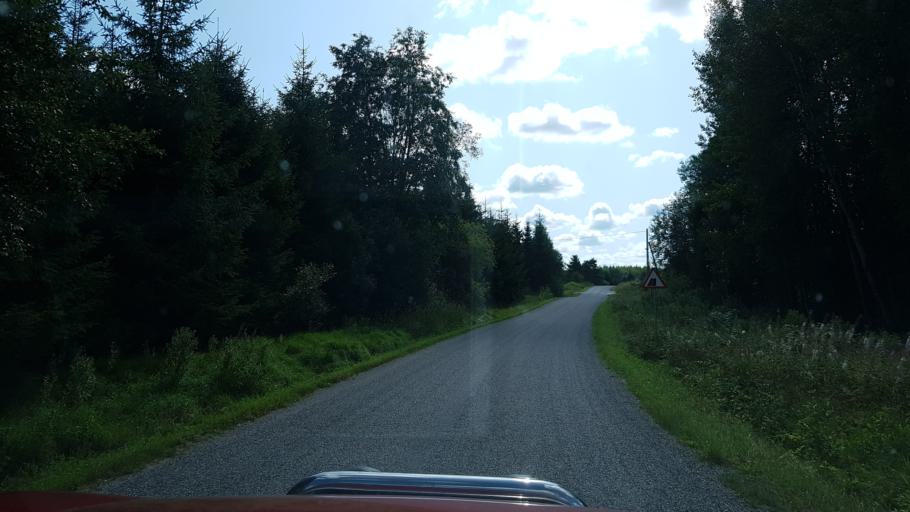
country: EE
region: Vorumaa
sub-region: Voru linn
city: Voru
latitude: 57.7079
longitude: 27.1905
